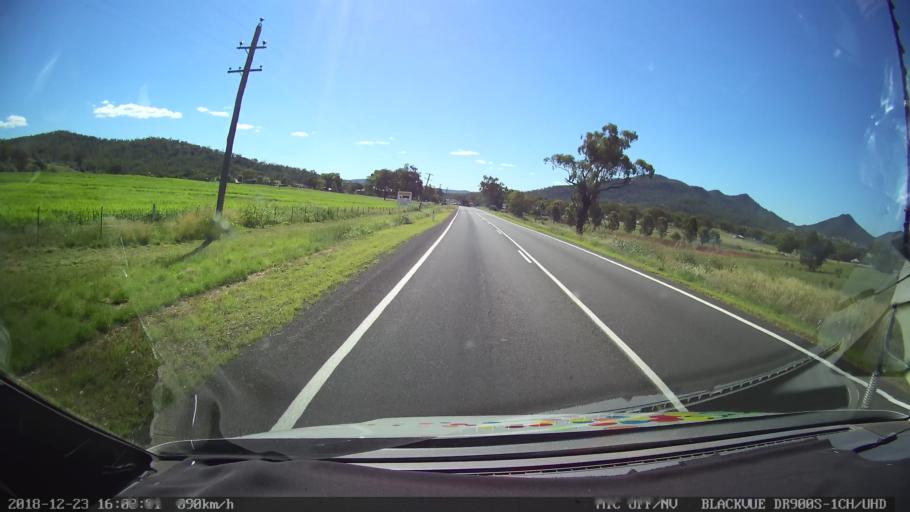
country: AU
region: New South Wales
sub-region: Tamworth Municipality
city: Phillip
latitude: -31.2668
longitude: 150.7537
